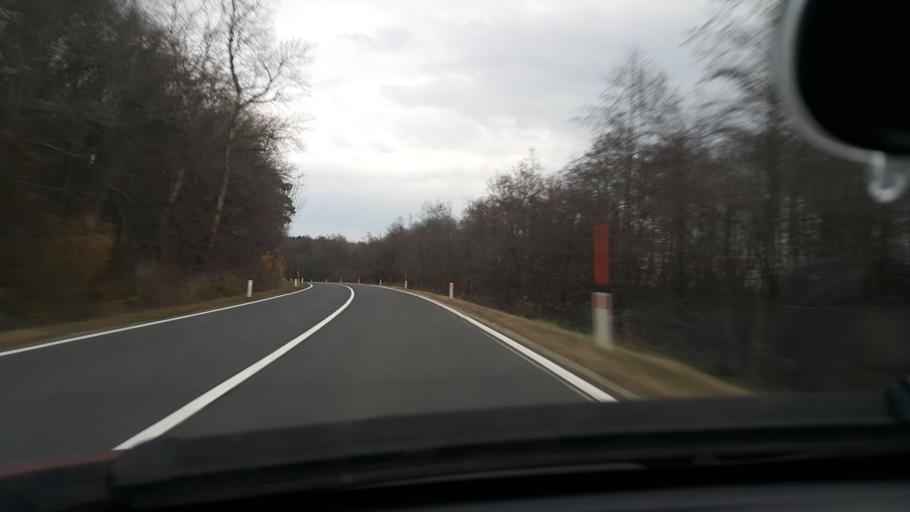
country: SI
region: Slovenska Bistrica
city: Zgornja Polskava
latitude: 46.3964
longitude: 15.6178
